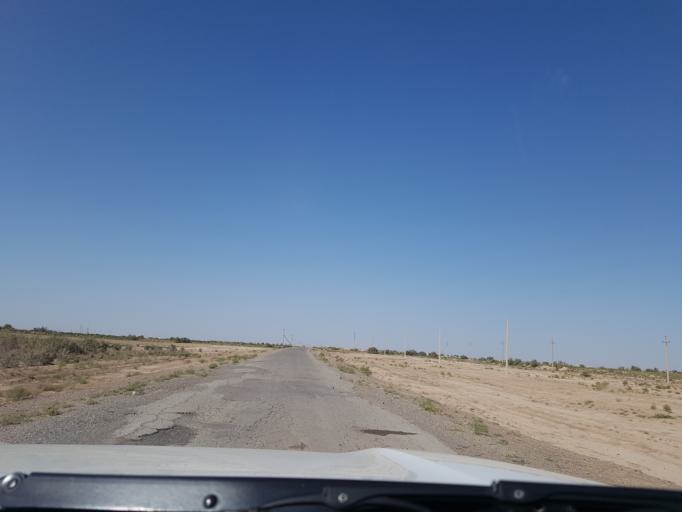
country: IR
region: Razavi Khorasan
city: Sarakhs
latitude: 36.4951
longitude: 61.2538
